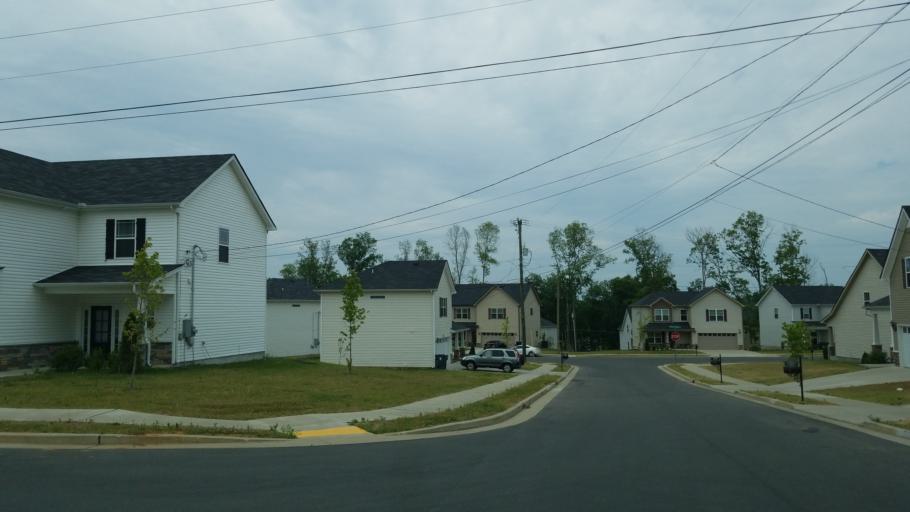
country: US
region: Tennessee
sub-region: Rutherford County
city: La Vergne
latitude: 36.0522
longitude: -86.6040
